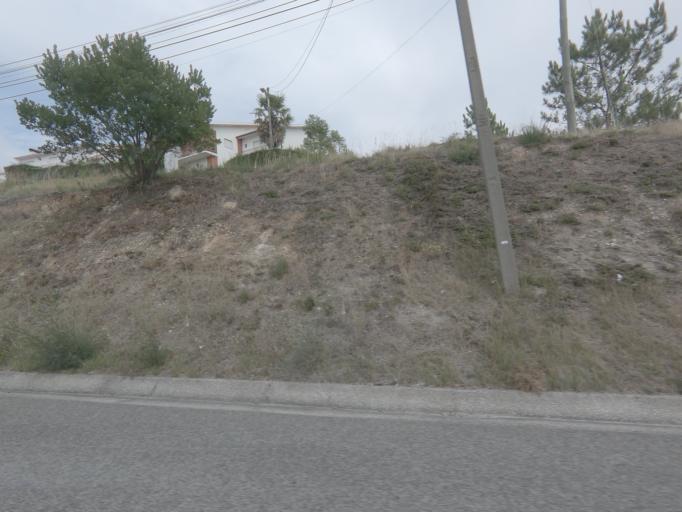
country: PT
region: Coimbra
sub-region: Condeixa-A-Nova
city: Condeixa-a-Nova
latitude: 40.1429
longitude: -8.4658
